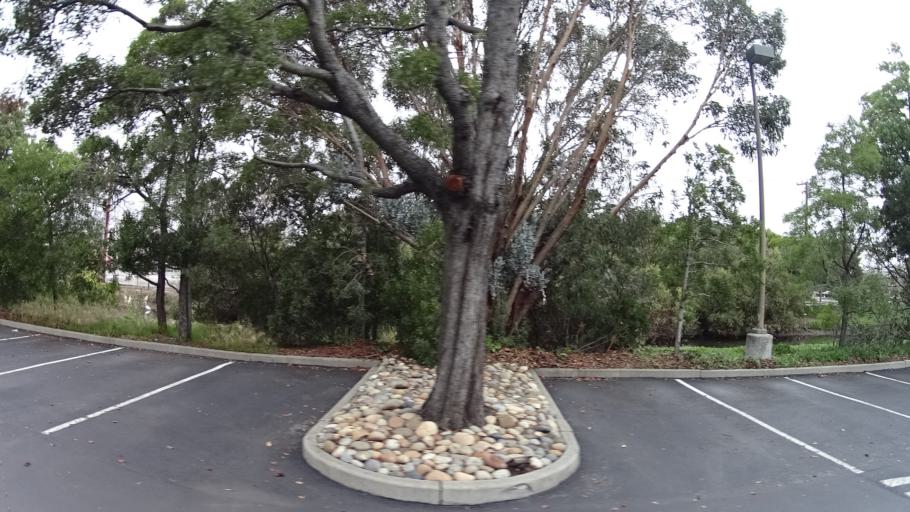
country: US
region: California
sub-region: San Mateo County
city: Foster City
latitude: 37.5515
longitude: -122.2915
